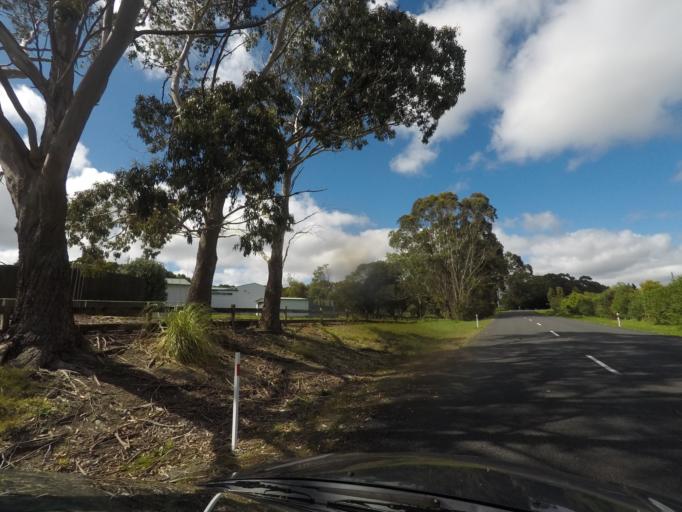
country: NZ
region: Auckland
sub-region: Auckland
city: Rothesay Bay
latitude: -36.7581
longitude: 174.6493
